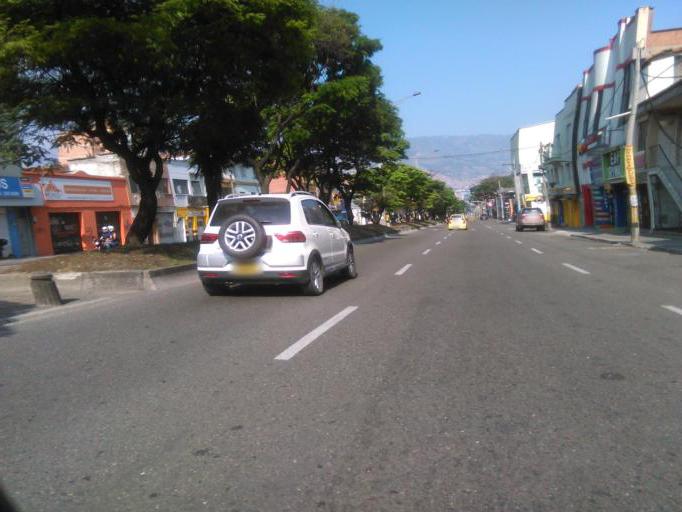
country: CO
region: Antioquia
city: Medellin
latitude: 6.2499
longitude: -75.5952
